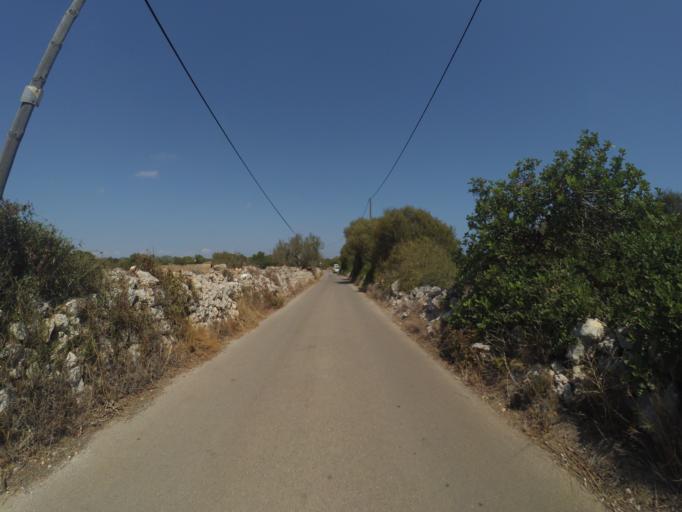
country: ES
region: Balearic Islands
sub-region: Illes Balears
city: Santanyi
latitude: 39.3928
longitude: 3.2369
